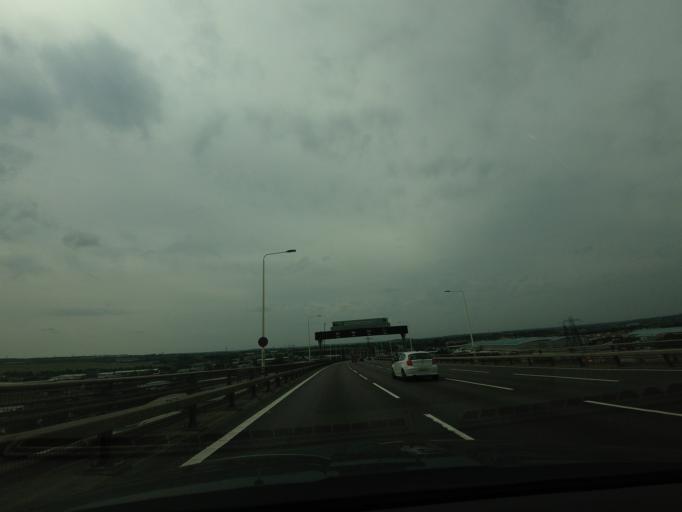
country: GB
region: England
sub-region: Kent
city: Stone
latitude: 51.4609
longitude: 0.2554
